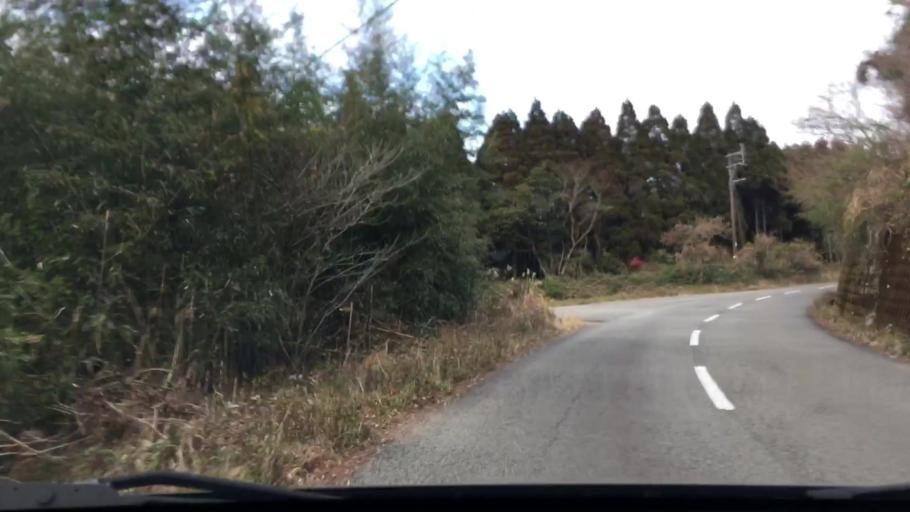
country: JP
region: Miyazaki
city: Nichinan
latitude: 31.6627
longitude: 131.3166
